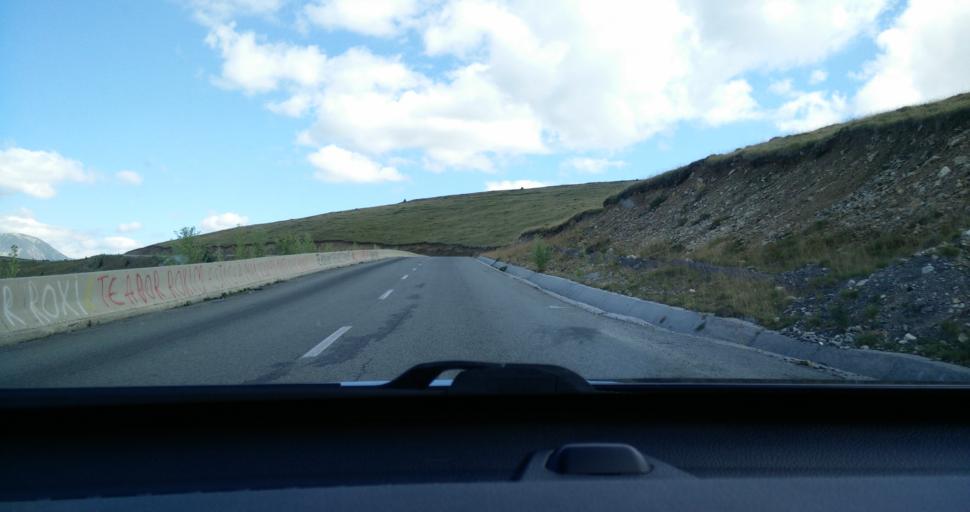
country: RO
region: Gorj
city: Novaci-Straini
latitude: 45.2546
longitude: 23.6975
